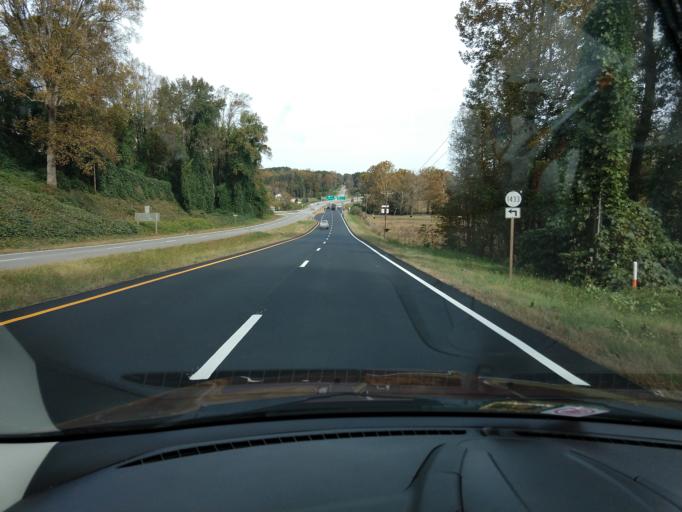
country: US
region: Virginia
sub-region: Pittsylvania County
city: Chatham
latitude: 36.8006
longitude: -79.3934
